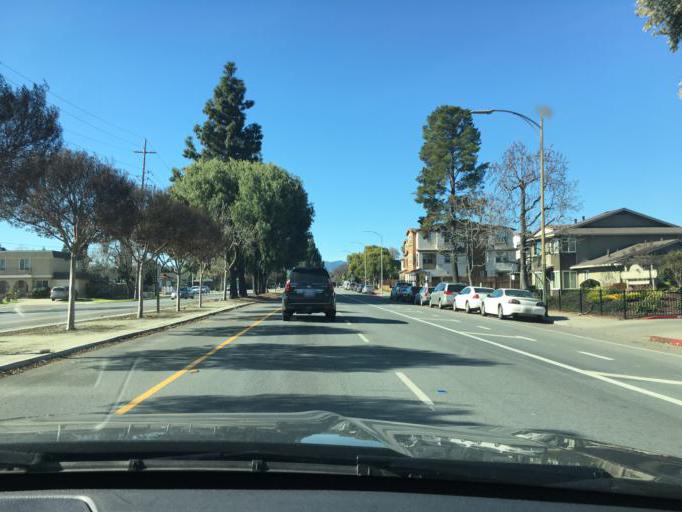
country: US
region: California
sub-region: Santa Clara County
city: Seven Trees
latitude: 37.2653
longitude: -121.8681
